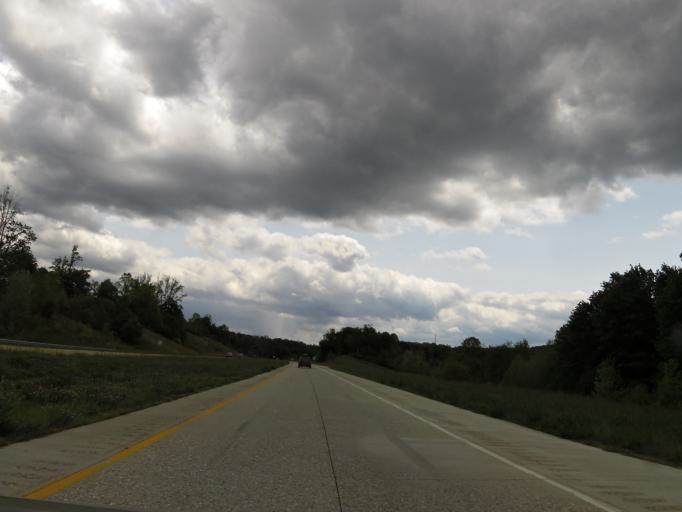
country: US
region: Ohio
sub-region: Meigs County
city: Pomeroy
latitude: 39.1510
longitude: -82.0299
